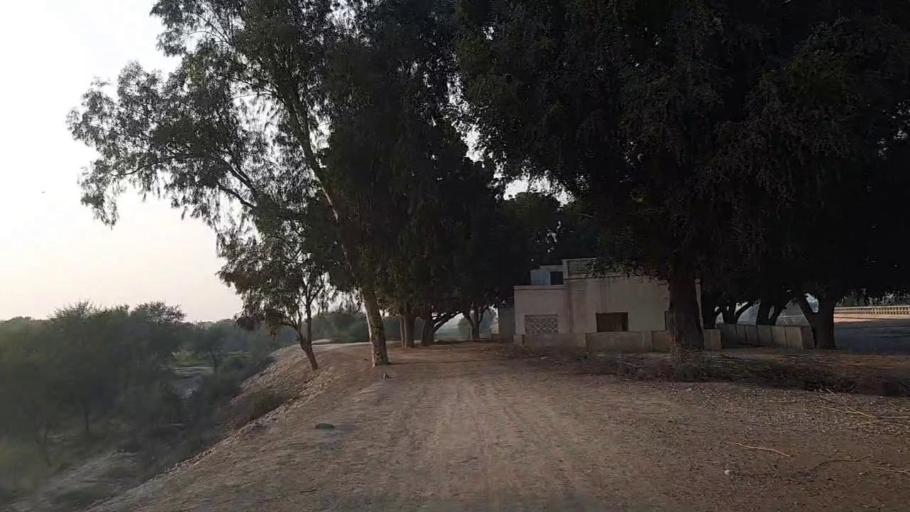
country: PK
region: Sindh
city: Sann
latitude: 26.1675
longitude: 68.1095
